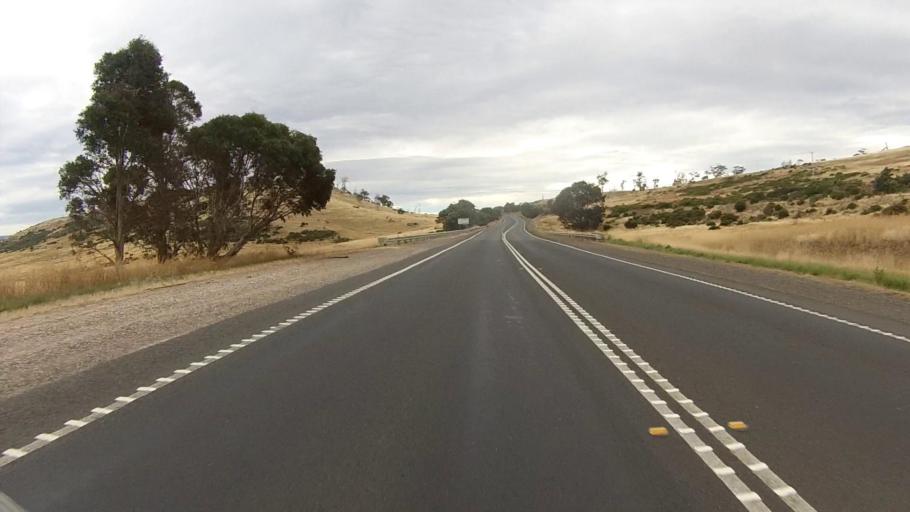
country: AU
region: Tasmania
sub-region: Brighton
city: Bridgewater
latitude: -42.3425
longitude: 147.3393
